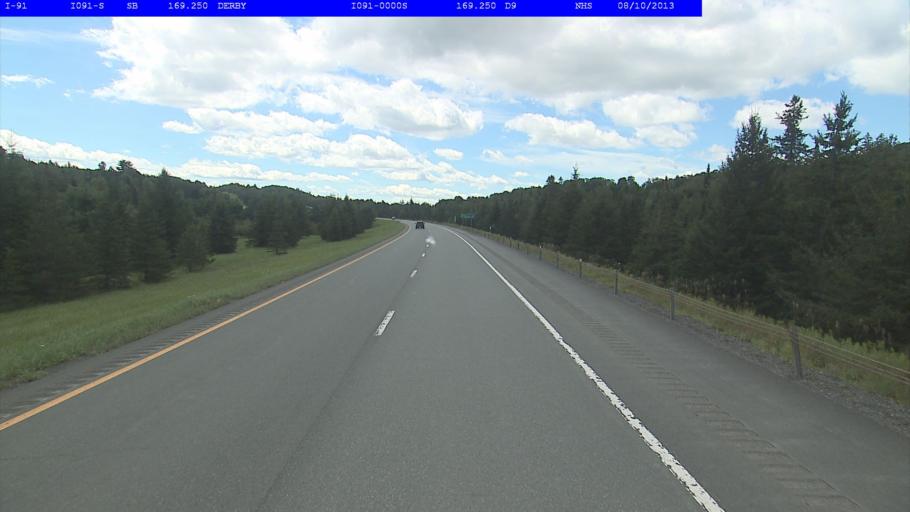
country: US
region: Vermont
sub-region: Orleans County
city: Newport
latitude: 44.9117
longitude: -72.1786
